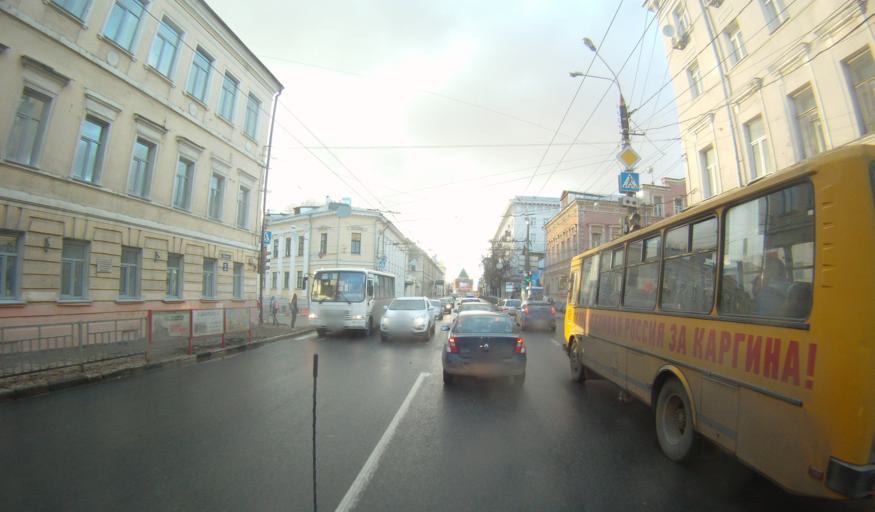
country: RU
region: Nizjnij Novgorod
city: Nizhniy Novgorod
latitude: 56.3240
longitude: 44.0092
